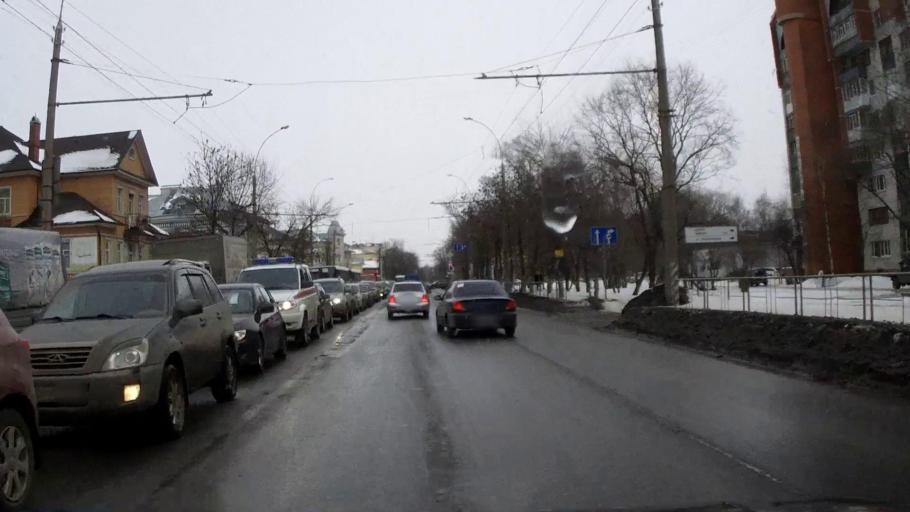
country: RU
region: Vologda
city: Vologda
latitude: 59.2199
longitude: 39.8688
